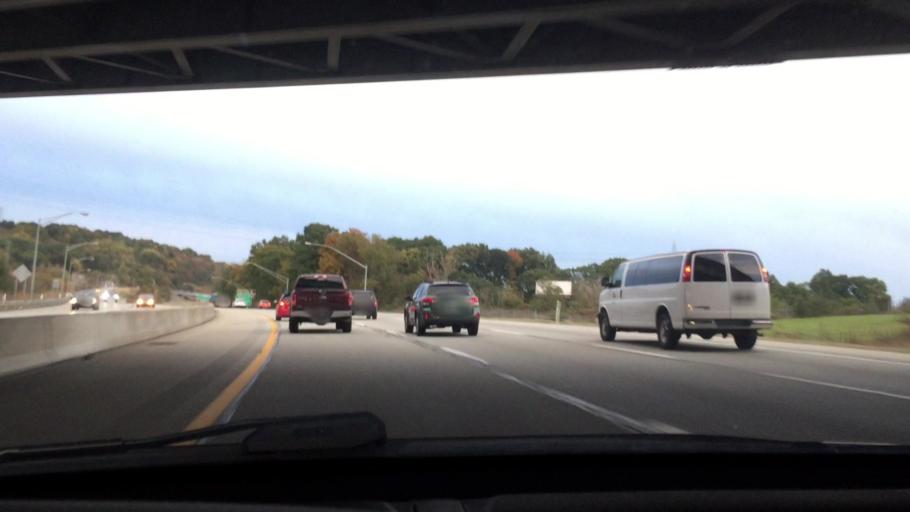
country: US
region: Pennsylvania
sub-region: Allegheny County
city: Cheswick
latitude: 40.5497
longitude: -79.8193
